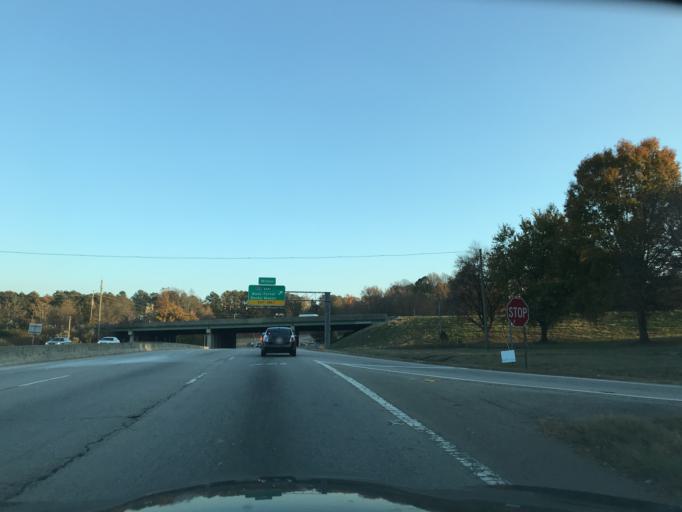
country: US
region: North Carolina
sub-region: Wake County
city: West Raleigh
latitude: 35.8362
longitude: -78.6710
